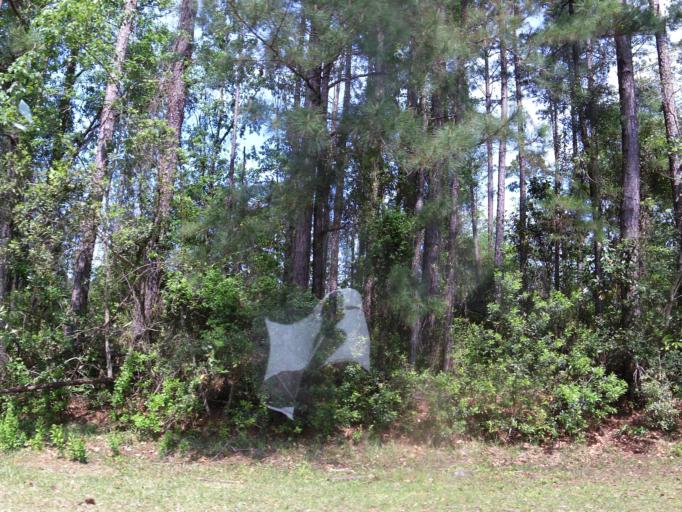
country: US
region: Georgia
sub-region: Camden County
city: Kingsland
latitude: 30.8085
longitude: -81.7508
